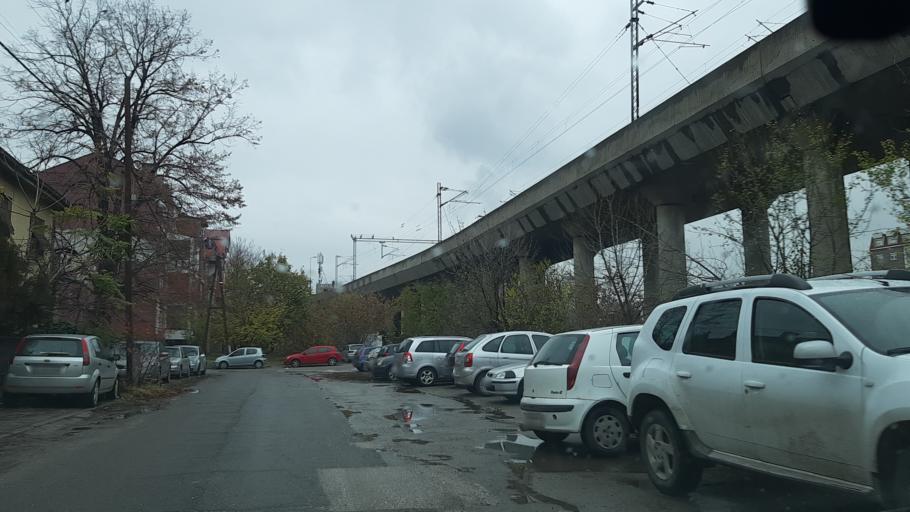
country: MK
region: Karpos
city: Skopje
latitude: 41.9882
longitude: 21.4425
